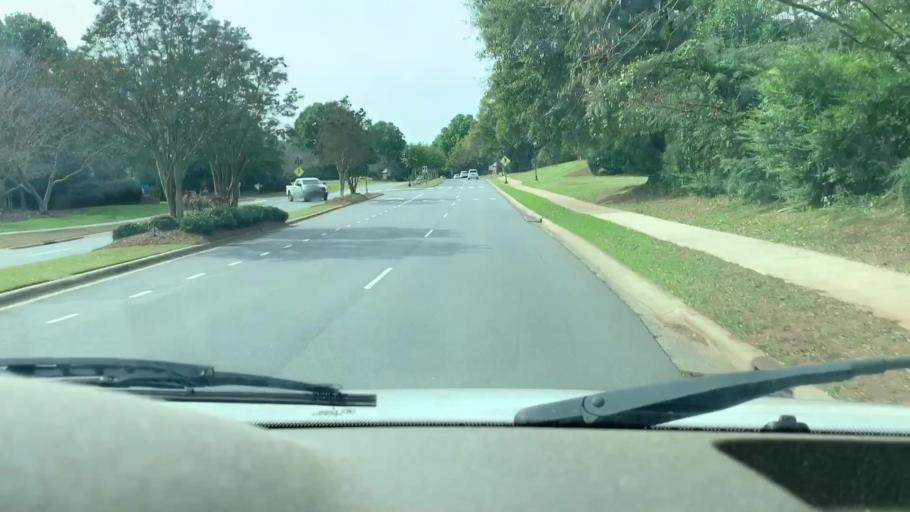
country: US
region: North Carolina
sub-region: Mecklenburg County
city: Cornelius
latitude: 35.4763
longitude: -80.8980
